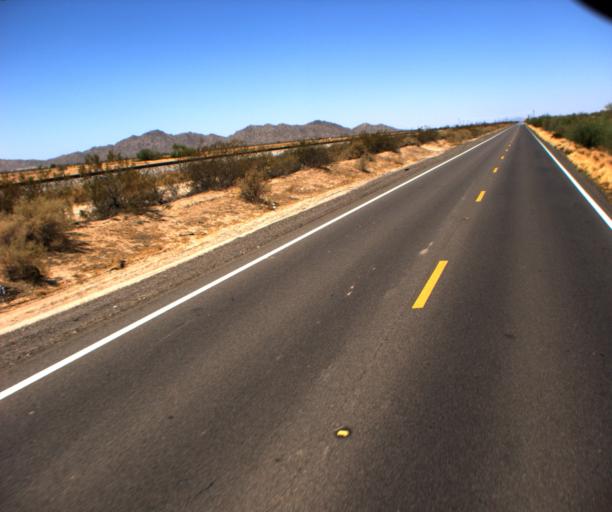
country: US
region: Arizona
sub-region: Pinal County
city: Maricopa
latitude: 33.0788
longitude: -112.1404
